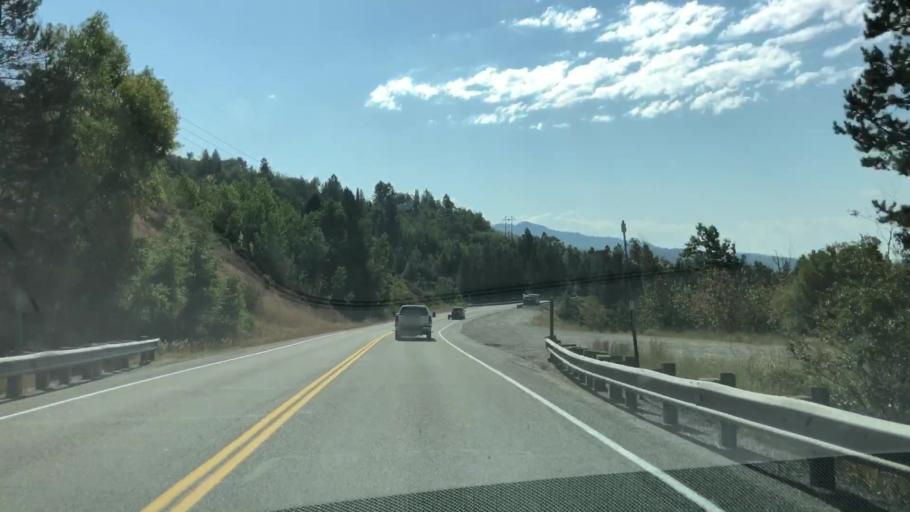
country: US
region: Idaho
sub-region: Teton County
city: Victor
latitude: 43.3081
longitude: -111.1374
